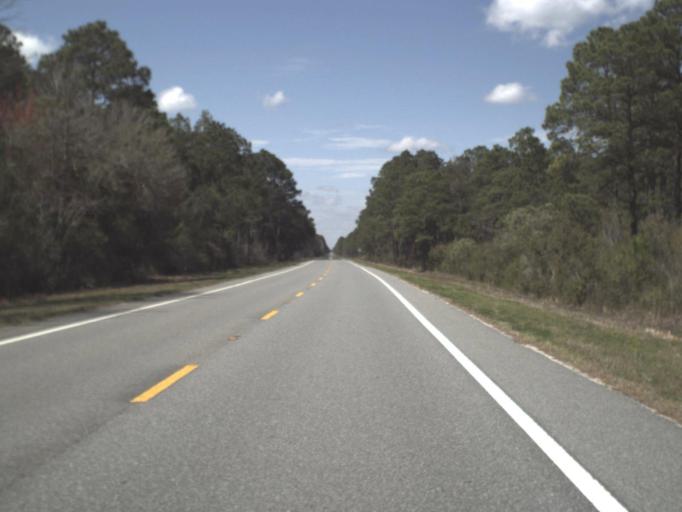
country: US
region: Florida
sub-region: Gadsden County
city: Midway
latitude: 30.3270
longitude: -84.4618
